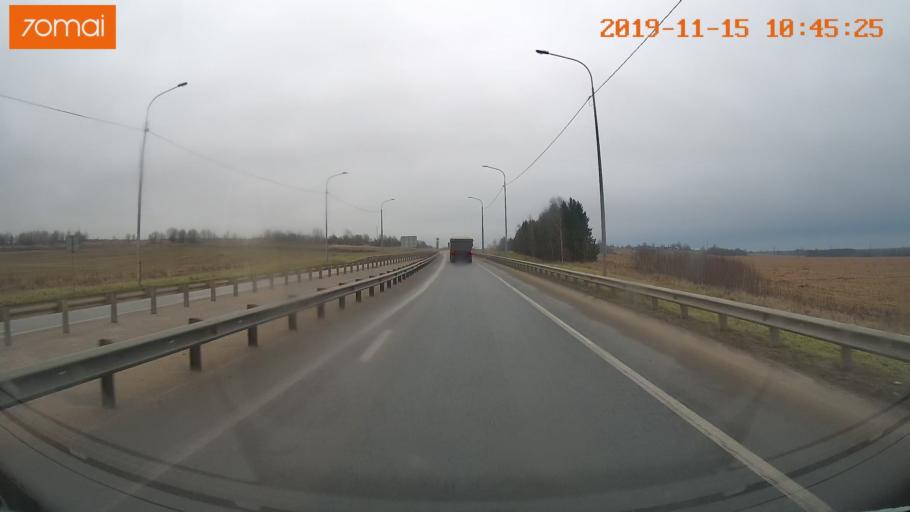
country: RU
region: Vologda
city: Sheksna
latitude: 59.2112
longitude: 38.5863
